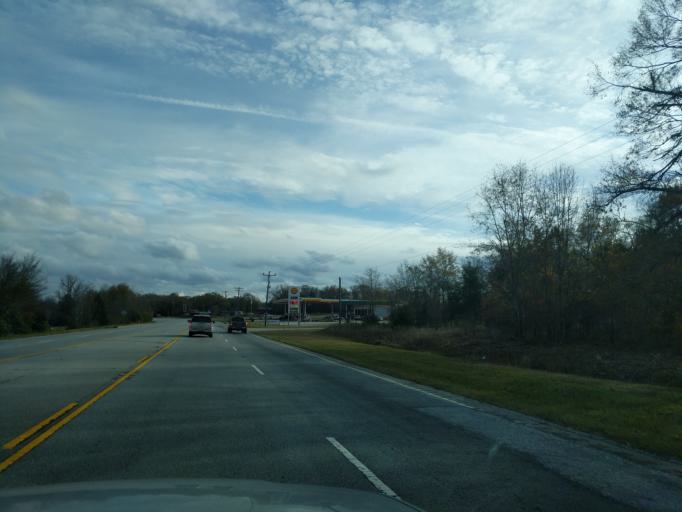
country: US
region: South Carolina
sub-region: Anderson County
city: Honea Path
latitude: 34.5142
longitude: -82.3081
